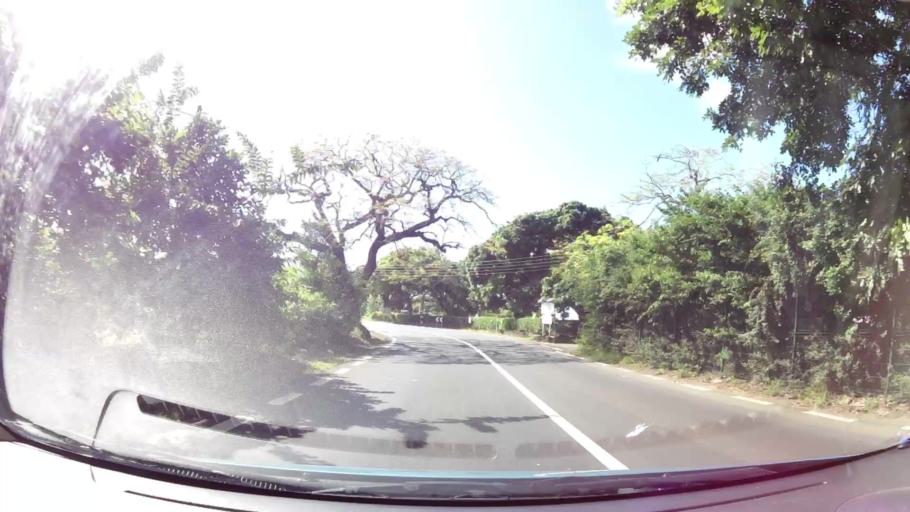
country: MU
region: Grand Port
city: Beau Vallon
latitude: -20.4238
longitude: 57.7007
